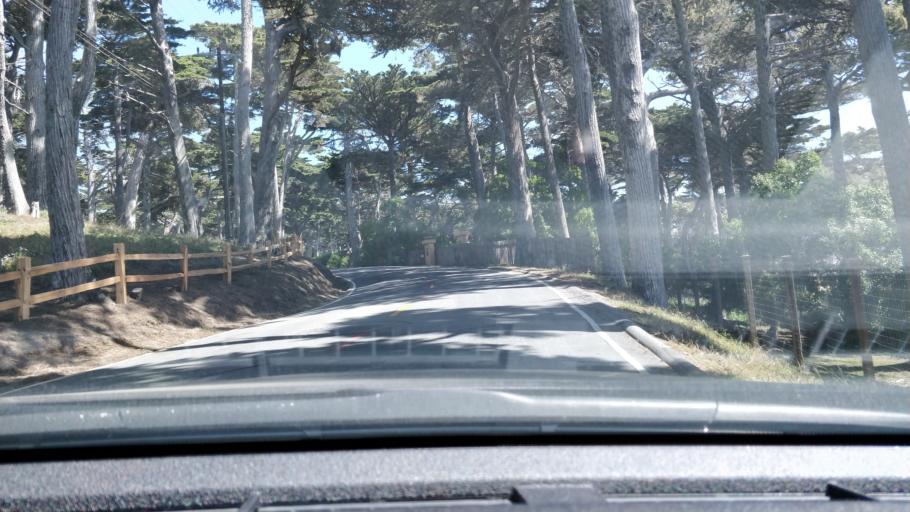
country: US
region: California
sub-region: Monterey County
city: Del Monte Forest
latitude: 36.5777
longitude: -121.9730
